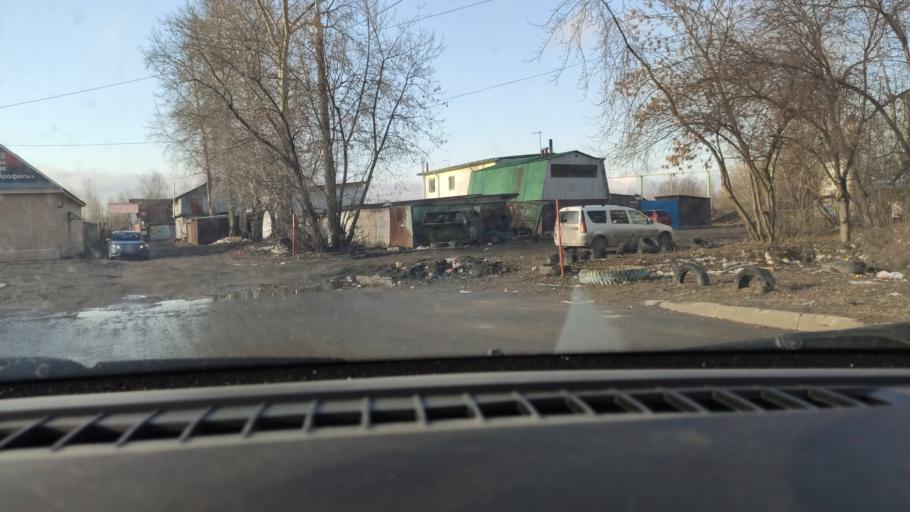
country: RU
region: Perm
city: Kondratovo
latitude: 58.0339
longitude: 56.0377
